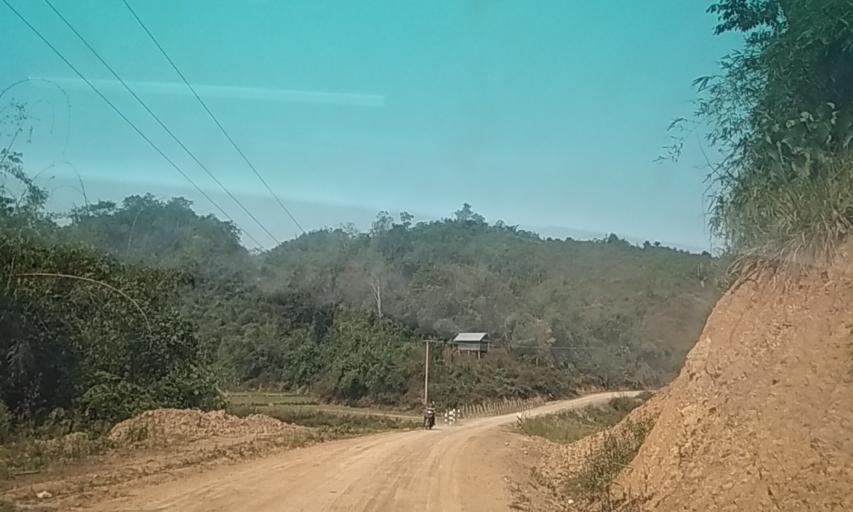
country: VN
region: Huyen Dien Bien
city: Dien Bien Phu
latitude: 21.4196
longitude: 102.7598
